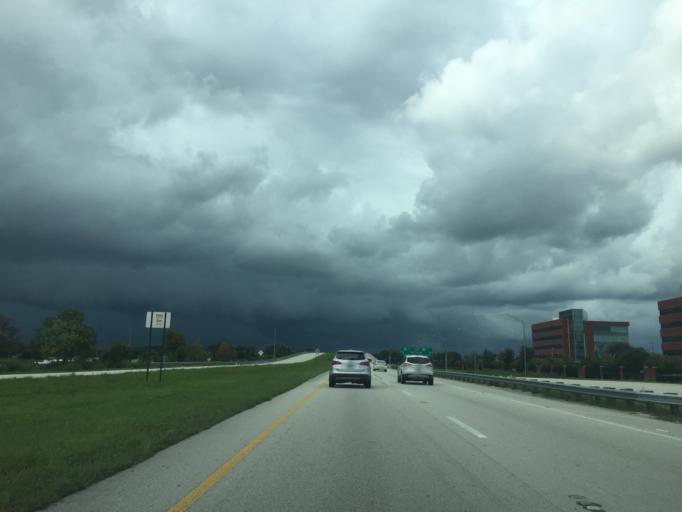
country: US
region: Florida
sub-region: Orange County
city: Lockhart
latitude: 28.6408
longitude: -81.4106
